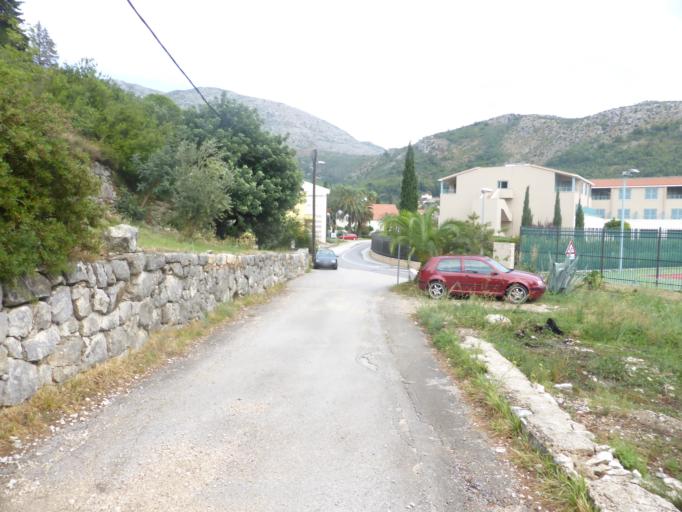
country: HR
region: Dubrovacko-Neretvanska
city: Podgora
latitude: 42.7882
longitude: 17.8879
